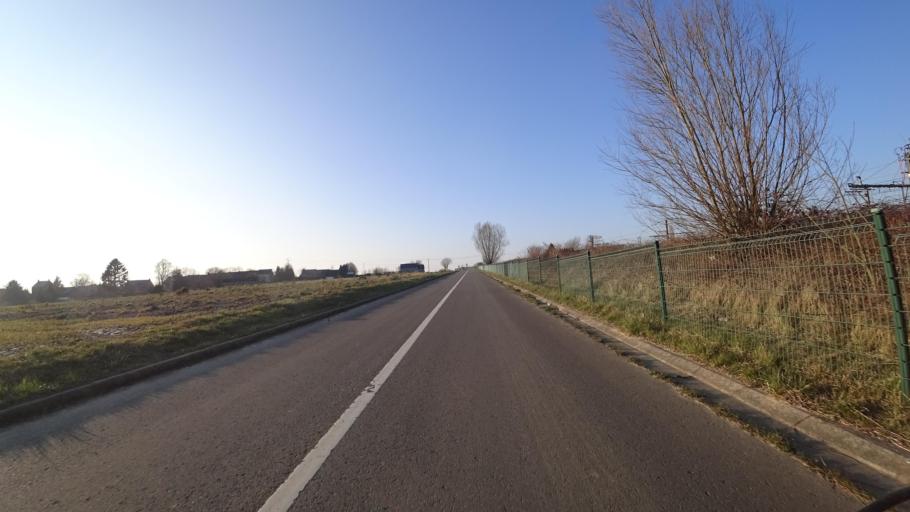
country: BE
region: Wallonia
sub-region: Province de Namur
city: Gembloux
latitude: 50.5762
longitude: 4.6848
